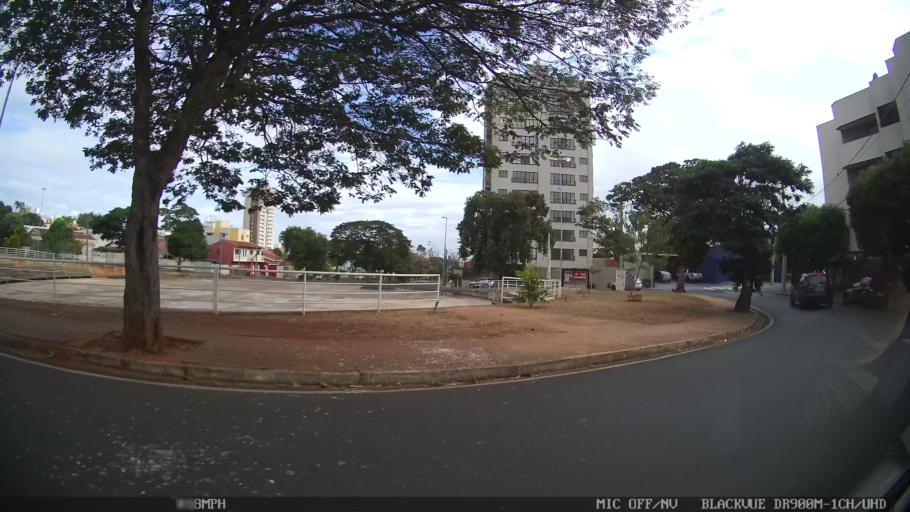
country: BR
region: Sao Paulo
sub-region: Sao Jose Do Rio Preto
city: Sao Jose do Rio Preto
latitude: -20.8353
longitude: -49.3812
